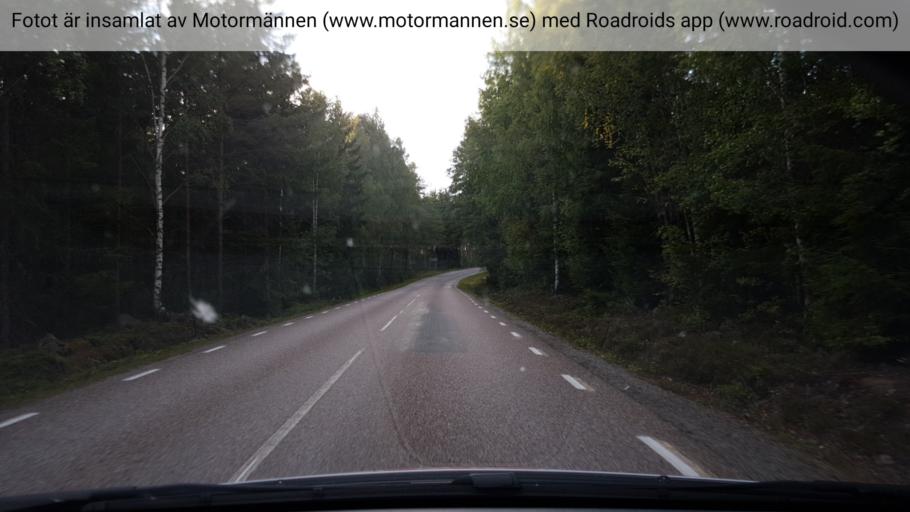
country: SE
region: Vaestmanland
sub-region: Vasteras
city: Skultuna
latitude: 59.7476
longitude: 16.3296
